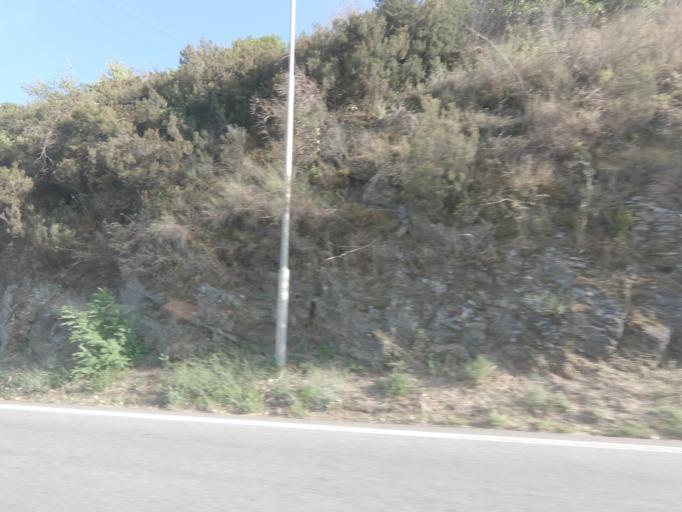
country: PT
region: Vila Real
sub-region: Peso da Regua
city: Peso da Regua
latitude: 41.1446
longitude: -7.7400
